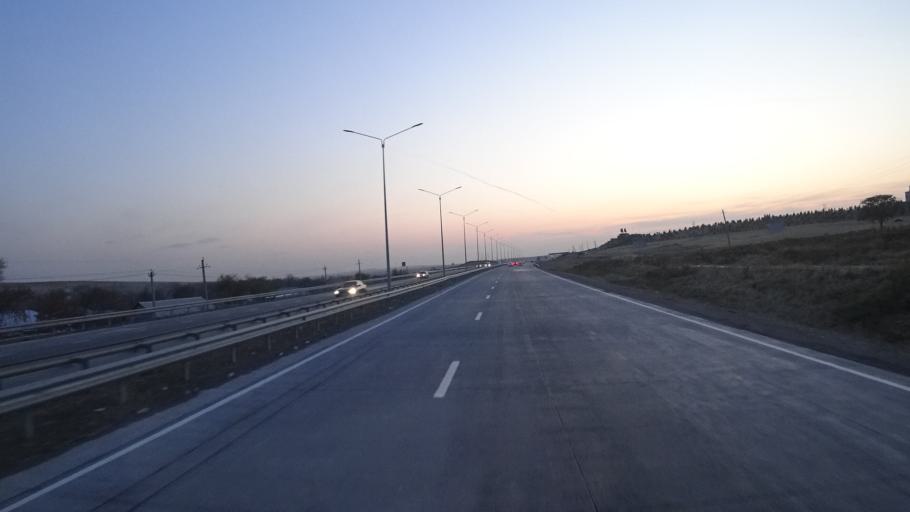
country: KZ
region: Ongtustik Qazaqstan
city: Qazyqurt
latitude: 41.8771
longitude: 69.4323
